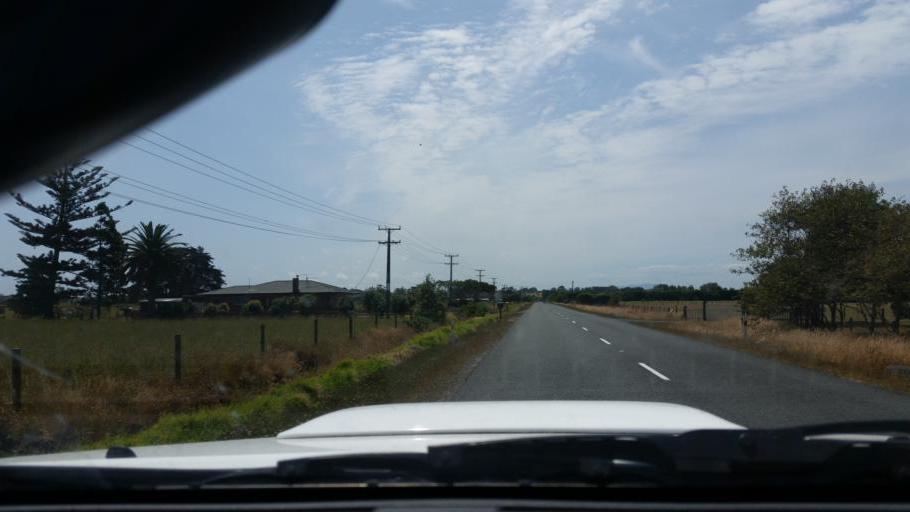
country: NZ
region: Northland
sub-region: Kaipara District
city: Dargaville
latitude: -36.0523
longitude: 173.9304
